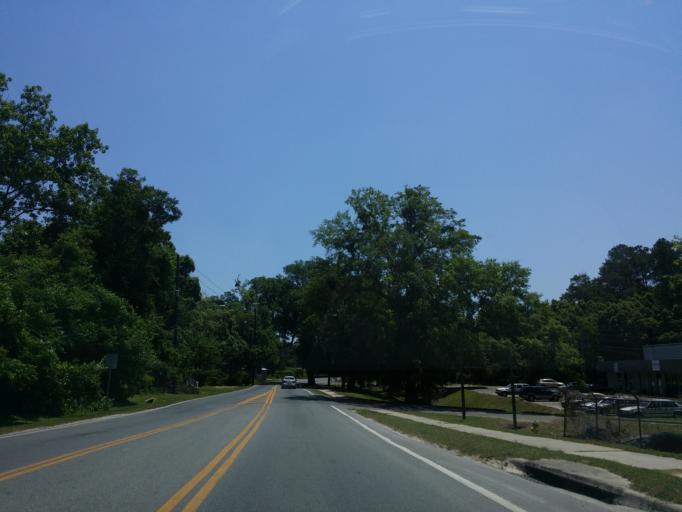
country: US
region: Florida
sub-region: Leon County
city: Tallahassee
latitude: 30.4627
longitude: -84.2986
